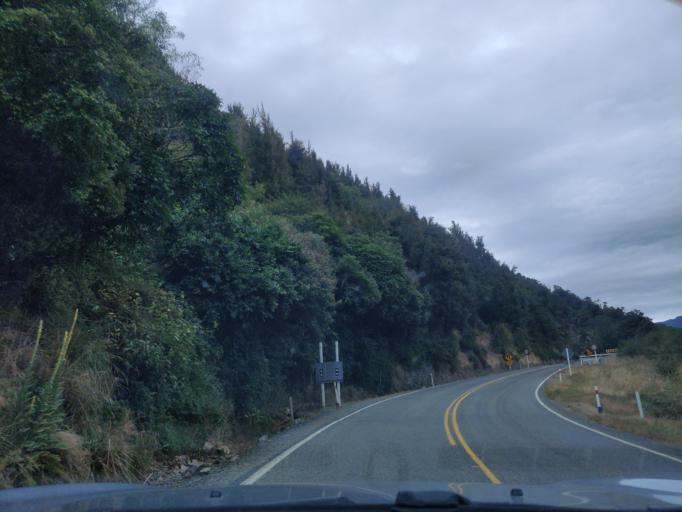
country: NZ
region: Tasman
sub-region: Tasman District
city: Wakefield
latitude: -41.6956
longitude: 172.6176
